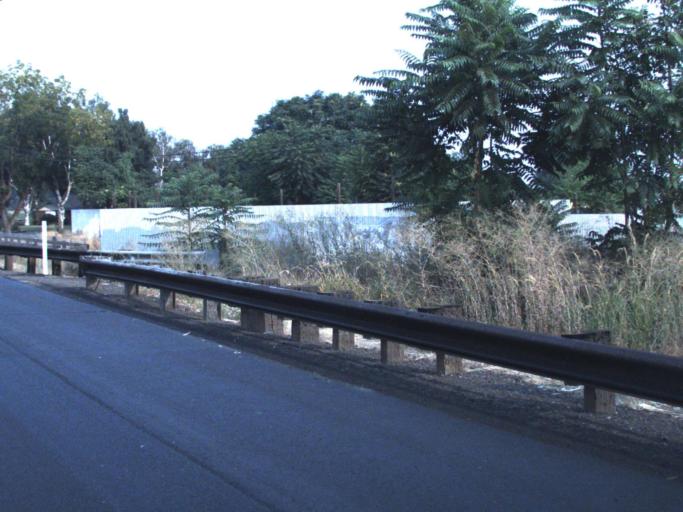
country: US
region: Washington
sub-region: Yakima County
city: Toppenish
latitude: 46.3970
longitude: -120.3687
